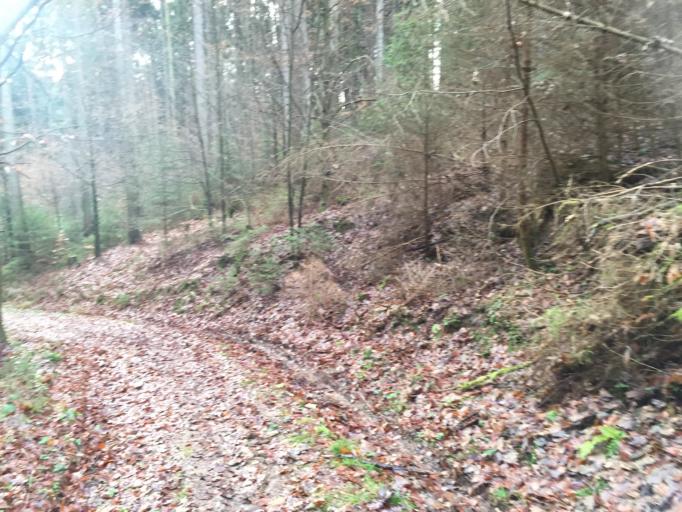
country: DE
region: Thuringia
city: Bollberg
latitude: 50.8897
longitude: 11.7923
